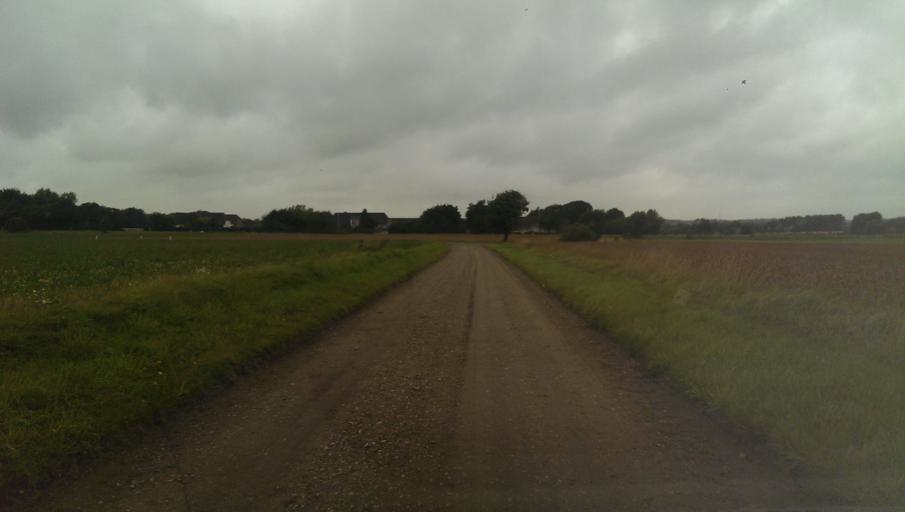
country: DK
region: South Denmark
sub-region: Esbjerg Kommune
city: Tjaereborg
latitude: 55.4882
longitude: 8.5976
